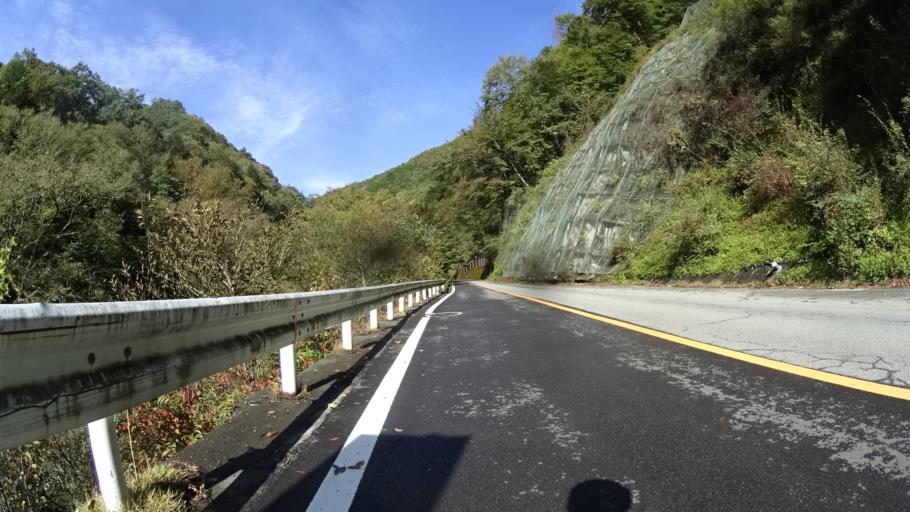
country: JP
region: Yamanashi
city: Enzan
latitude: 35.8041
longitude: 138.8509
